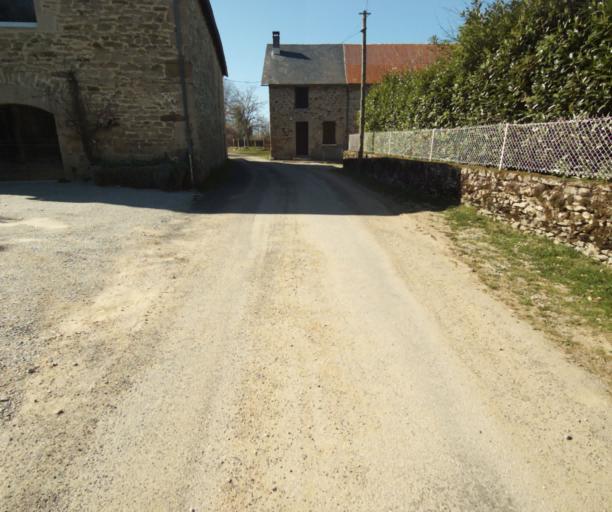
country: FR
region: Limousin
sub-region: Departement de la Correze
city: Treignac
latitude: 45.4780
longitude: 1.7682
